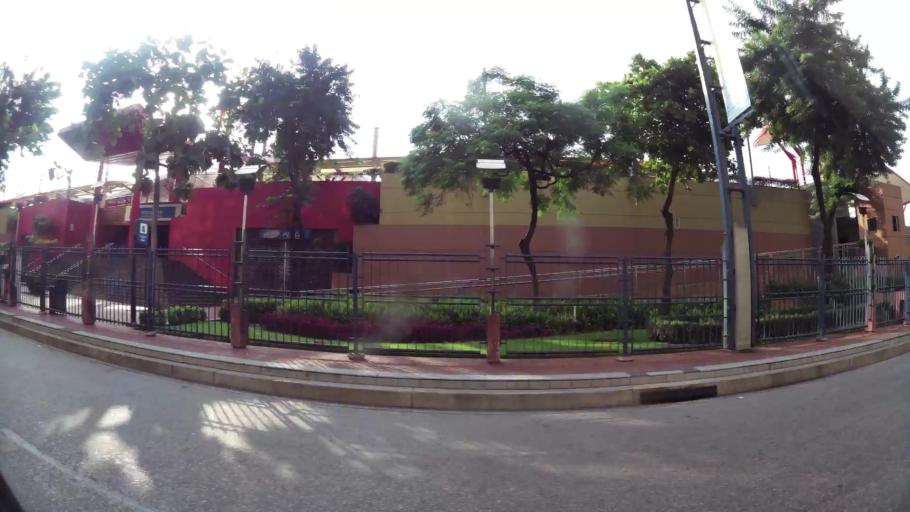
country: EC
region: Guayas
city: Guayaquil
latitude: -2.1991
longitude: -79.8814
